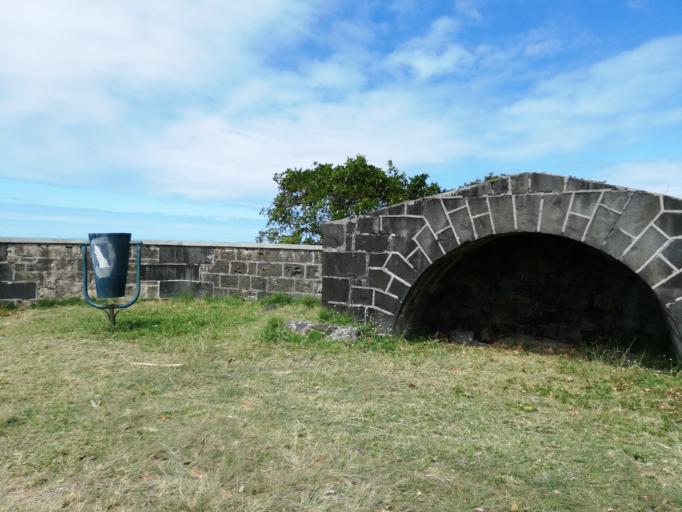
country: MU
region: Grand Port
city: Bambous Virieux
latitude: -20.3375
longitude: 57.7793
